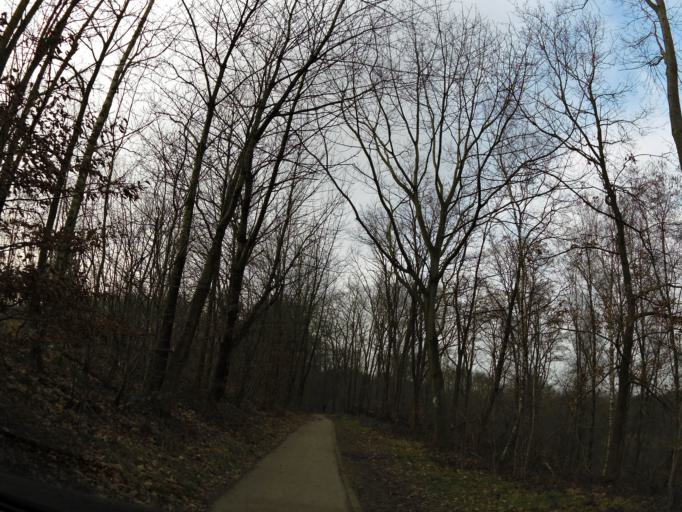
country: NL
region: Limburg
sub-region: Gemeente Kerkrade
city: Kerkrade
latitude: 50.9304
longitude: 6.0414
